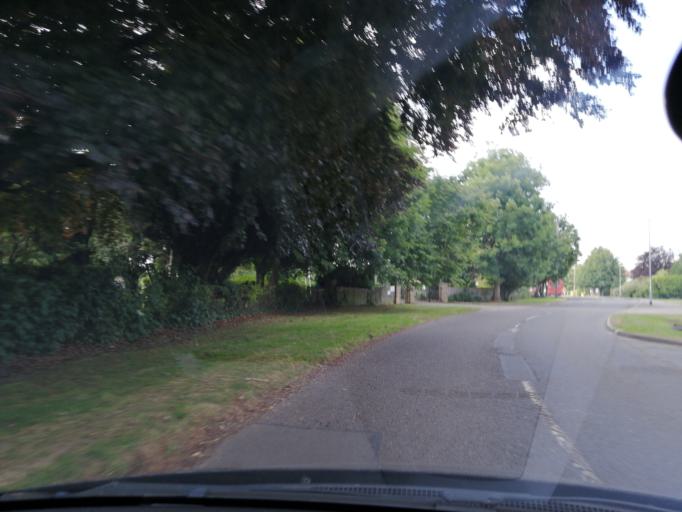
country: GB
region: England
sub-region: Cambridgeshire
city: Yaxley
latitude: 52.5135
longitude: -0.2700
